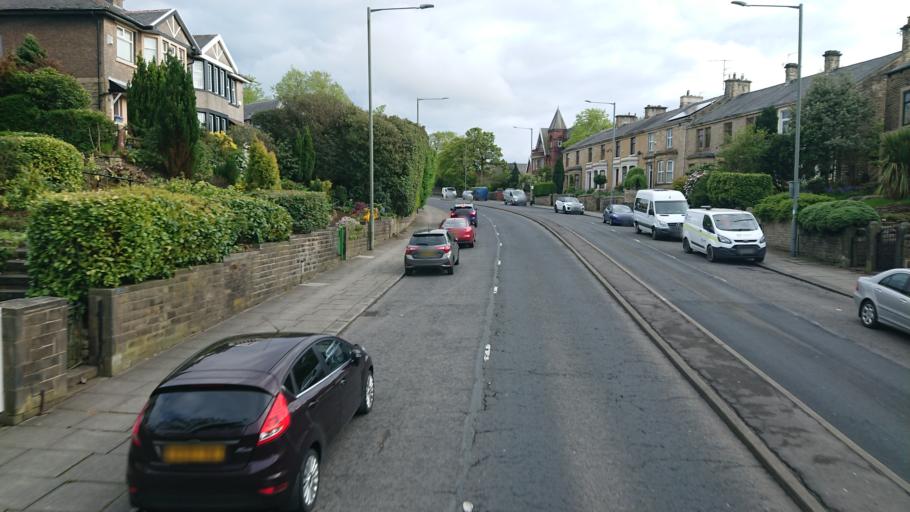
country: GB
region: England
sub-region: Lancashire
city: Burnley
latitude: 53.7801
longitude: -2.2542
